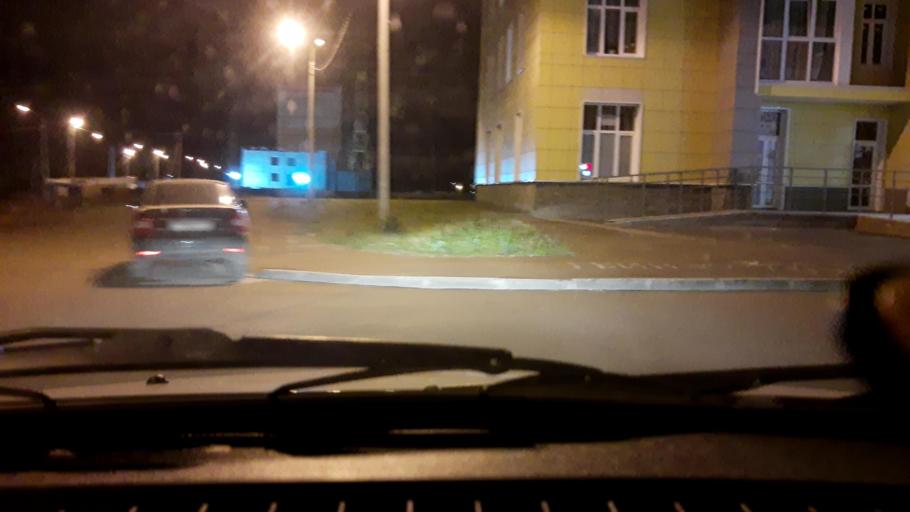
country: RU
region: Bashkortostan
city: Ufa
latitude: 54.6841
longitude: 55.9838
